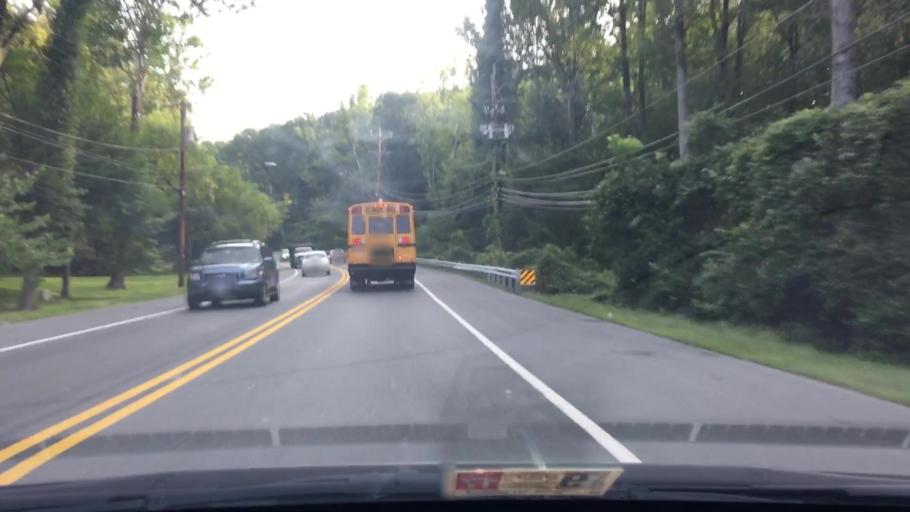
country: US
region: Maryland
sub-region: Montgomery County
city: North Bethesda
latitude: 39.0341
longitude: -77.1600
